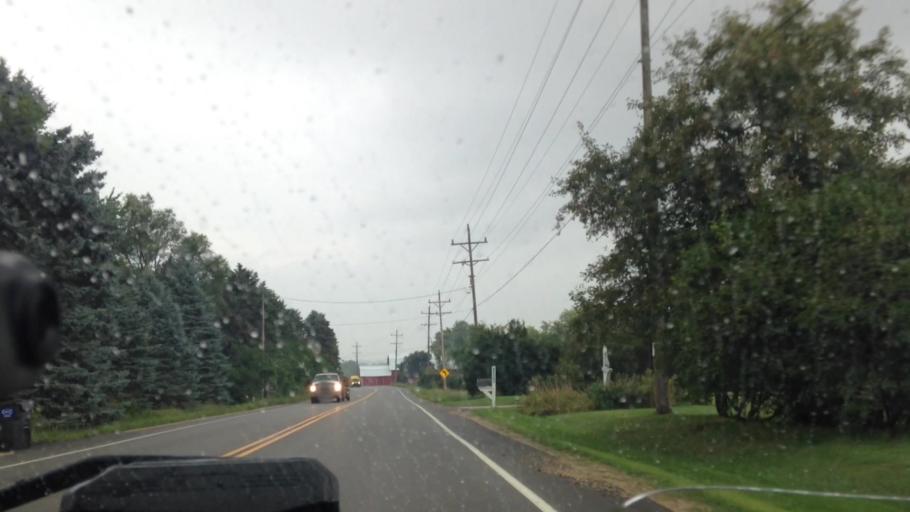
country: US
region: Wisconsin
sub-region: Washington County
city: Richfield
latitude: 43.2778
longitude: -88.2099
